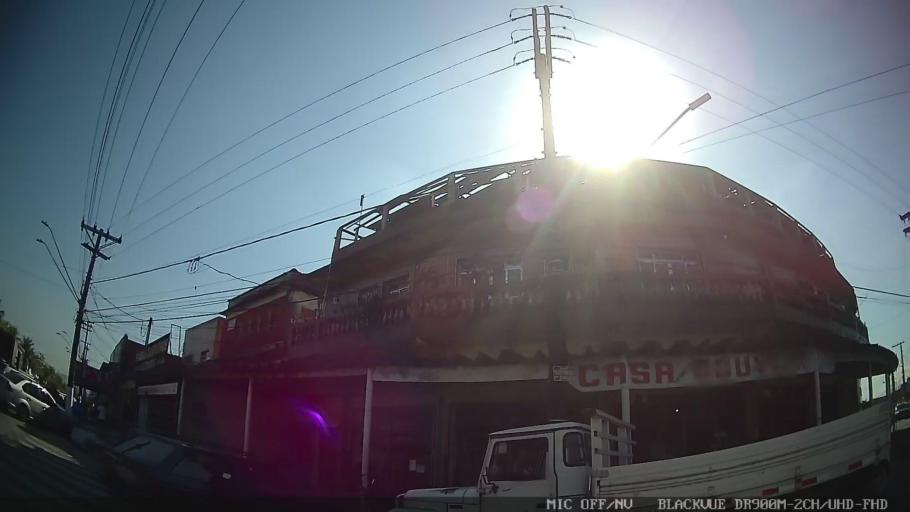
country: BR
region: Sao Paulo
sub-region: Santos
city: Santos
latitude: -23.9476
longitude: -46.2969
